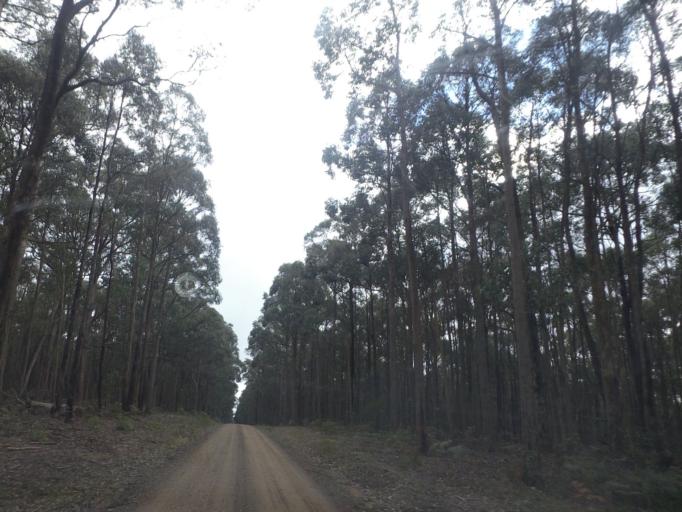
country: AU
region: Victoria
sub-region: Moorabool
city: Bacchus Marsh
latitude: -37.4306
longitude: 144.3132
